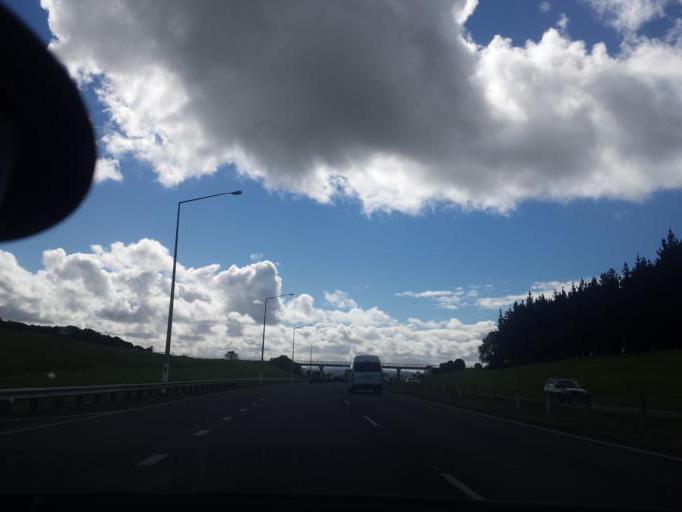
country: NZ
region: Auckland
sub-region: Auckland
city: Rothesay Bay
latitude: -36.6540
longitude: 174.6641
